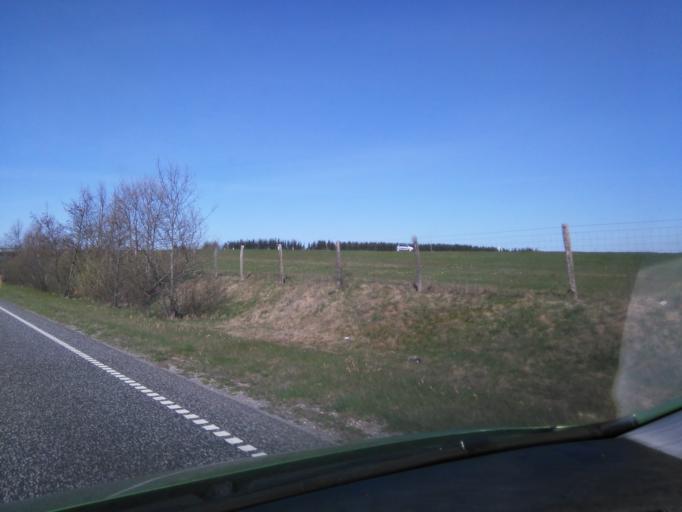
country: DK
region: Central Jutland
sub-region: Hedensted Kommune
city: Torring
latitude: 55.8419
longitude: 9.5443
